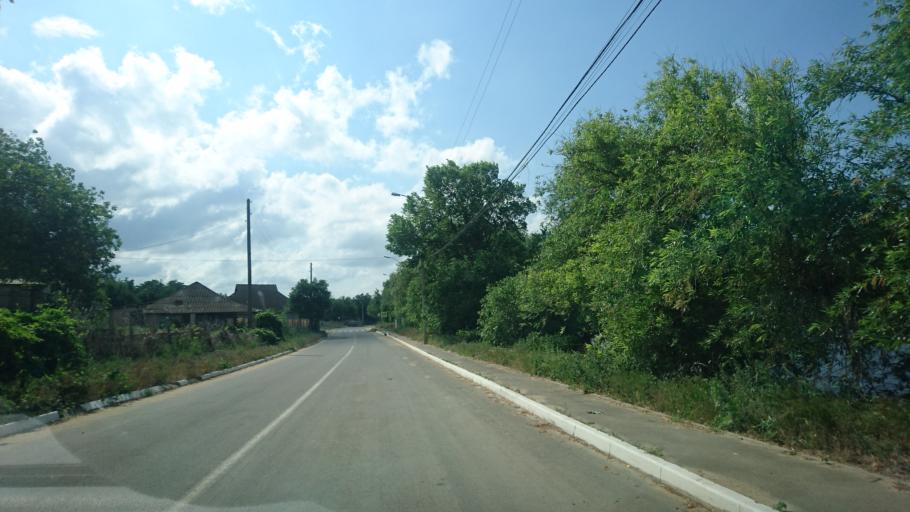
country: MD
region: Telenesti
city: Cocieri
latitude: 47.3533
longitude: 29.1066
